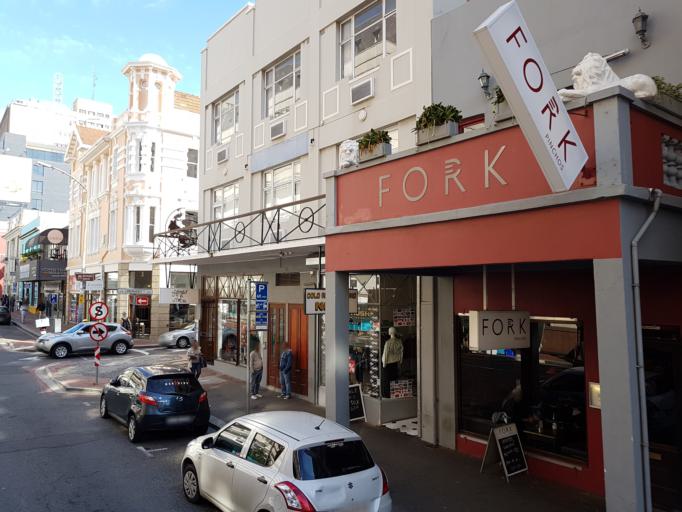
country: ZA
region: Western Cape
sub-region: City of Cape Town
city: Cape Town
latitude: -33.9223
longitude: 18.4194
